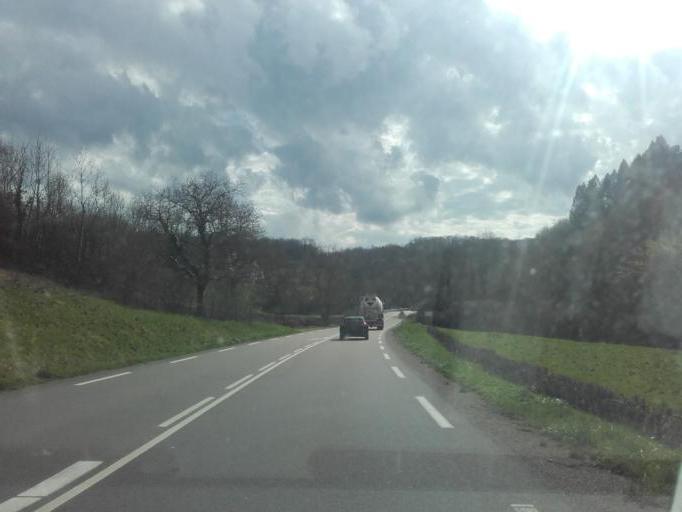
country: FR
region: Bourgogne
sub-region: Departement de la Cote-d'Or
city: Nolay
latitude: 46.9623
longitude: 4.6909
